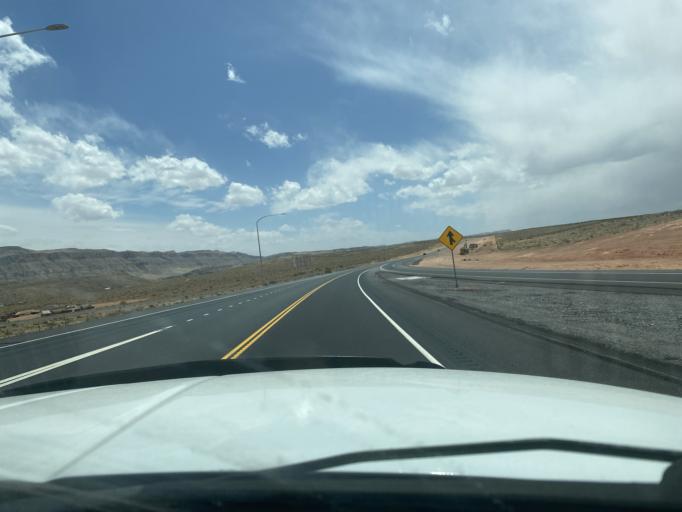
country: US
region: Utah
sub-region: Washington County
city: Hurricane
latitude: 37.1228
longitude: -113.3438
